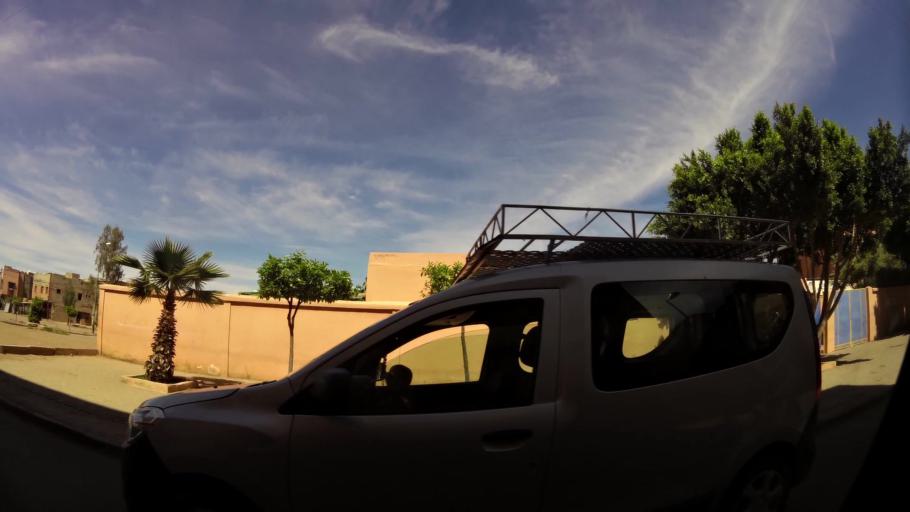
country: MA
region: Marrakech-Tensift-Al Haouz
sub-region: Marrakech
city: Marrakesh
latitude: 31.5984
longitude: -7.9601
